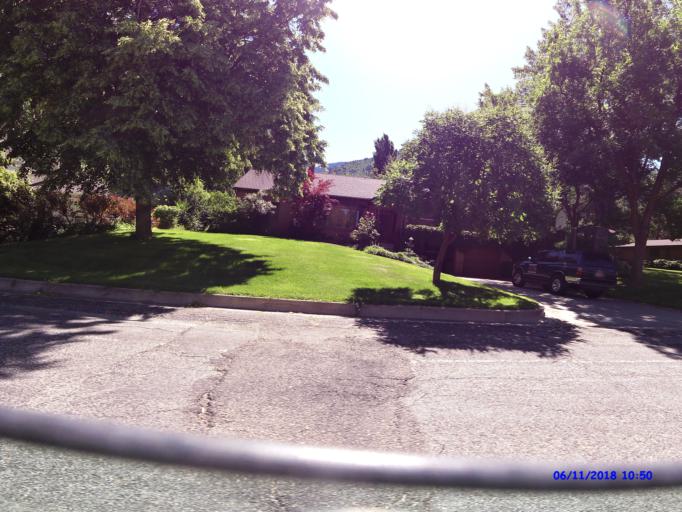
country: US
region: Utah
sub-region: Weber County
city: Ogden
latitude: 41.2129
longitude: -111.9371
